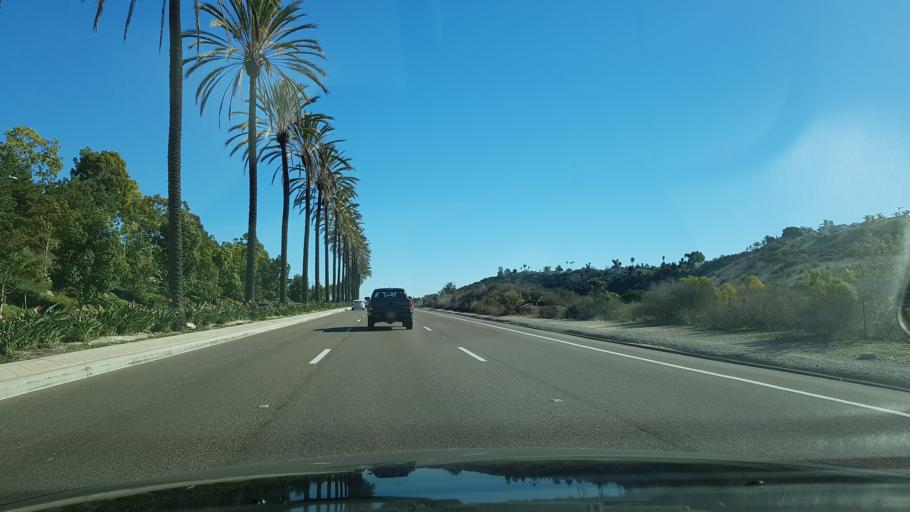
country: US
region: California
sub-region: San Diego County
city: Vista
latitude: 33.2037
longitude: -117.3041
